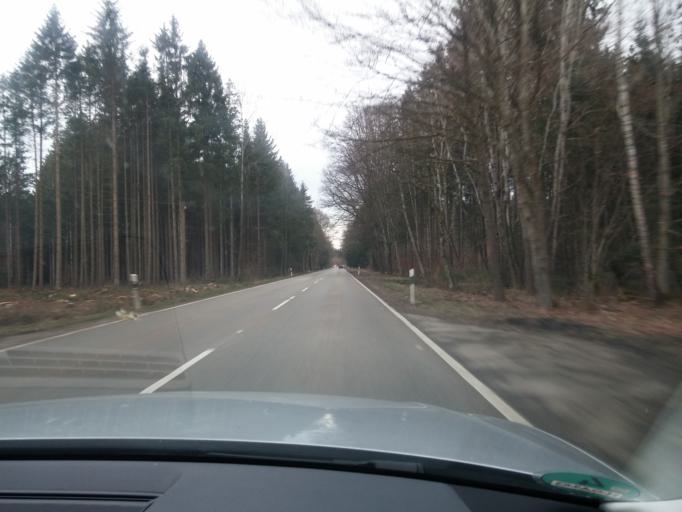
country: DE
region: Bavaria
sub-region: Upper Bavaria
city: Oberpframmern
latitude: 48.0328
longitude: 11.7910
